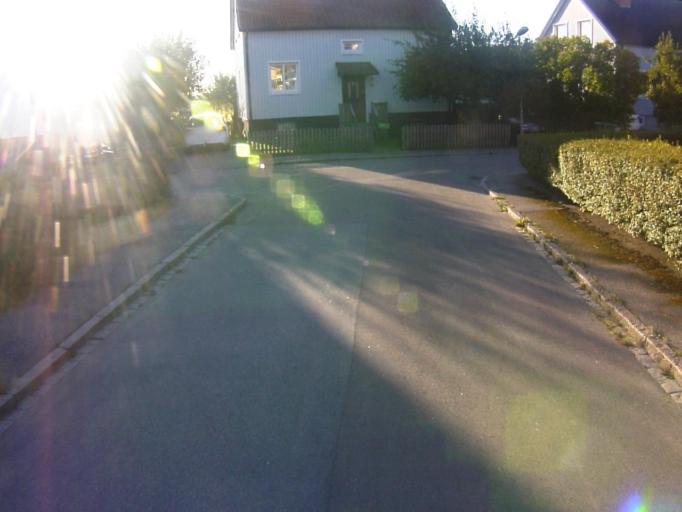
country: SE
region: Soedermanland
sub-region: Eskilstuna Kommun
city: Eskilstuna
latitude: 59.3790
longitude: 16.5317
